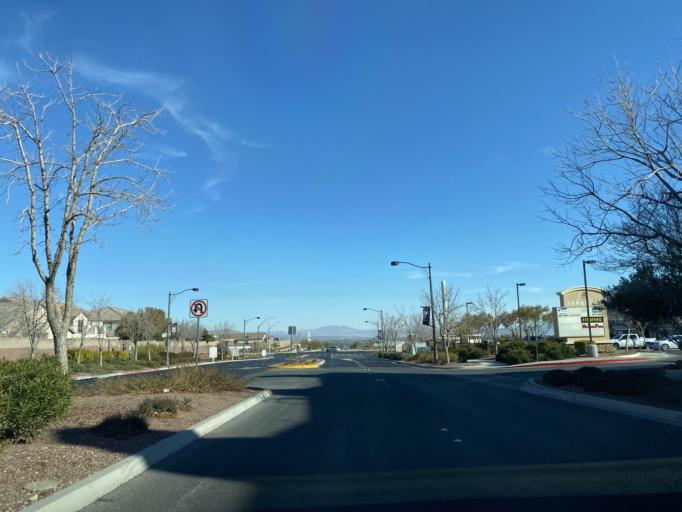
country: US
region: Nevada
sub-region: Clark County
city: Summerlin South
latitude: 36.2920
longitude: -115.3169
